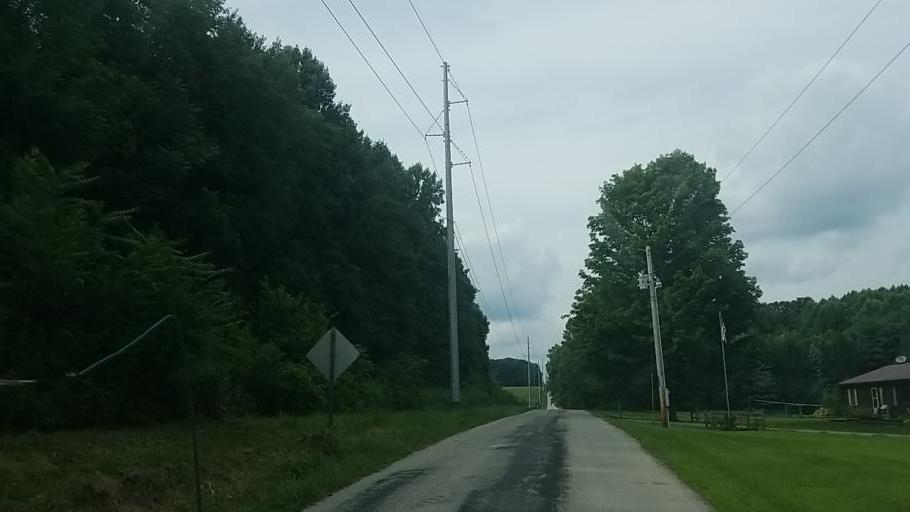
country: US
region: Ohio
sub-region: Knox County
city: Fredericktown
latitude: 40.5506
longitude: -82.5474
